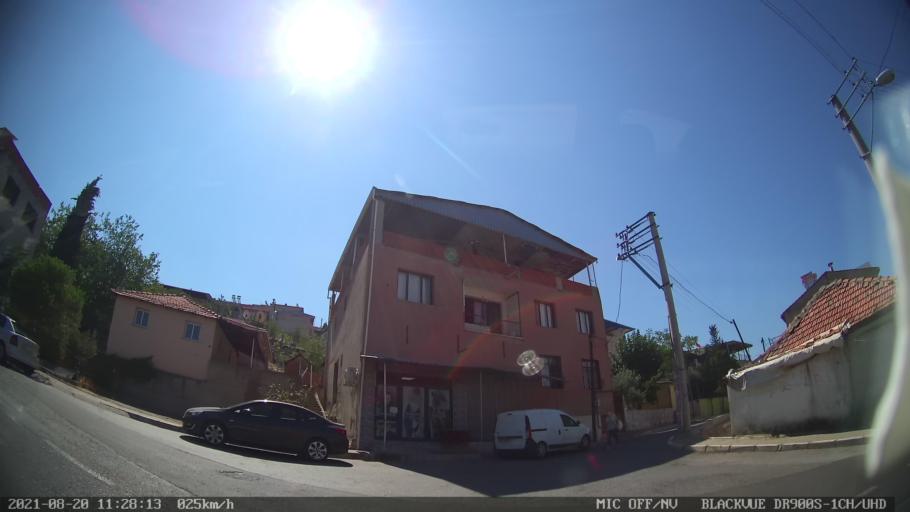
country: TR
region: Izmir
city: Karsiyaka
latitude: 38.5007
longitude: 27.0722
